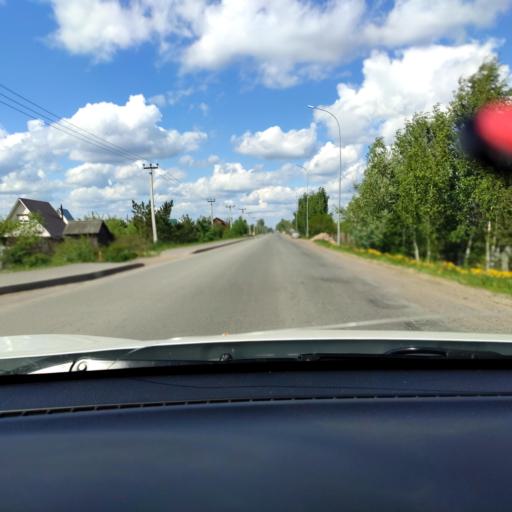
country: RU
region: Tatarstan
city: Stolbishchi
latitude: 55.6962
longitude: 49.1945
